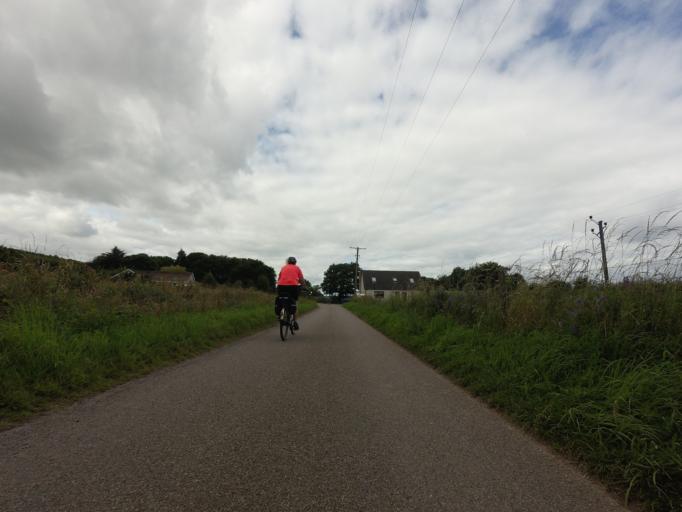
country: GB
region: Scotland
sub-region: Moray
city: Kinloss
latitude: 57.6346
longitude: -3.5224
